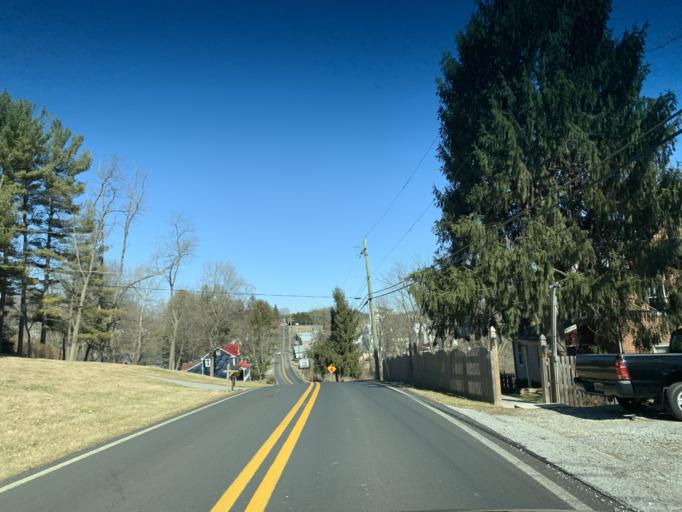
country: US
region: Maryland
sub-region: Carroll County
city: Manchester
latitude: 39.6172
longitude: -76.8970
